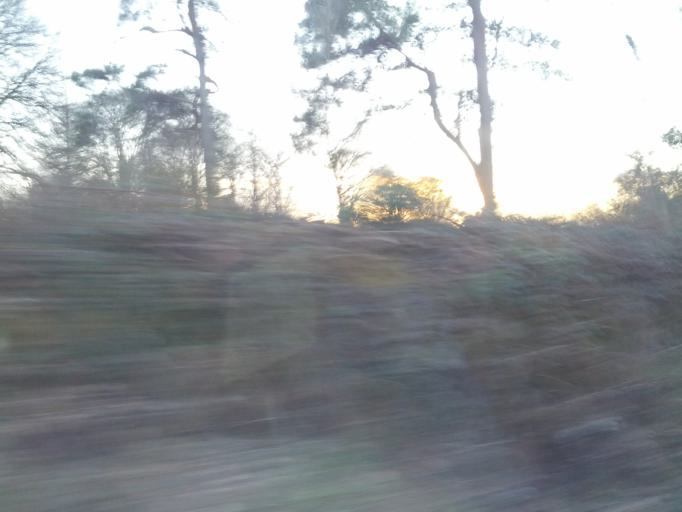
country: IE
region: Connaught
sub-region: County Galway
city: Athenry
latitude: 53.2798
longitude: -8.7602
